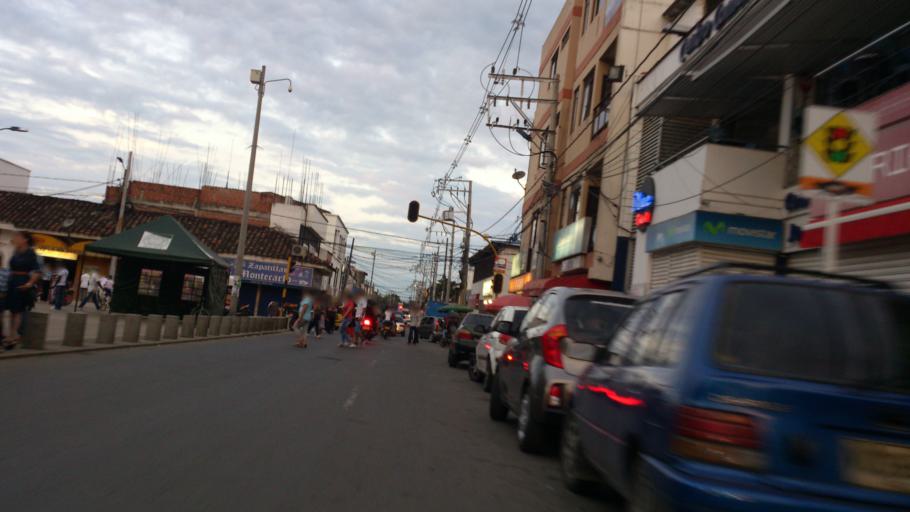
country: CO
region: Valle del Cauca
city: Jamundi
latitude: 3.2615
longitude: -76.5405
